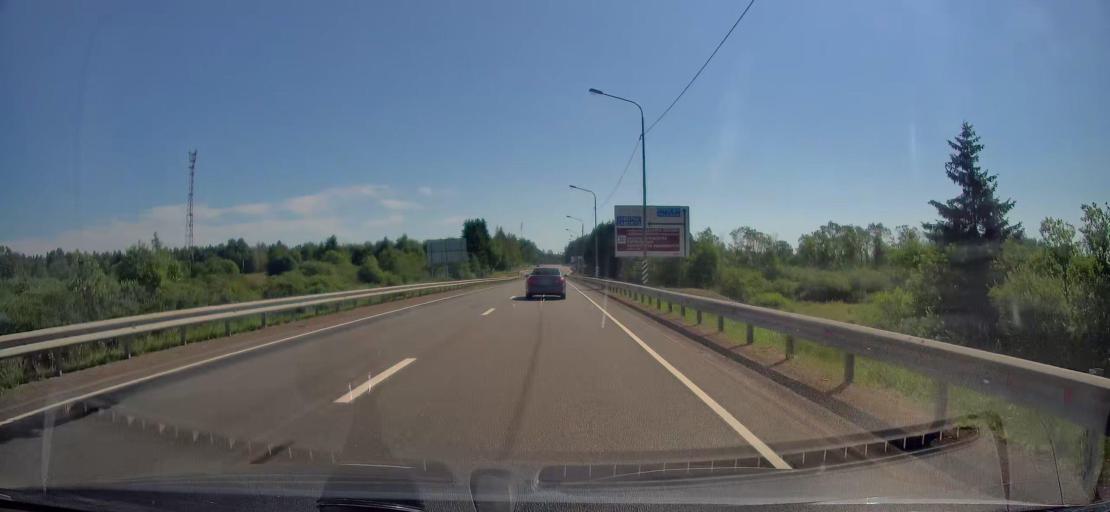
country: RU
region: Leningrad
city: Yefimovskiy
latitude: 59.3468
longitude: 34.8520
